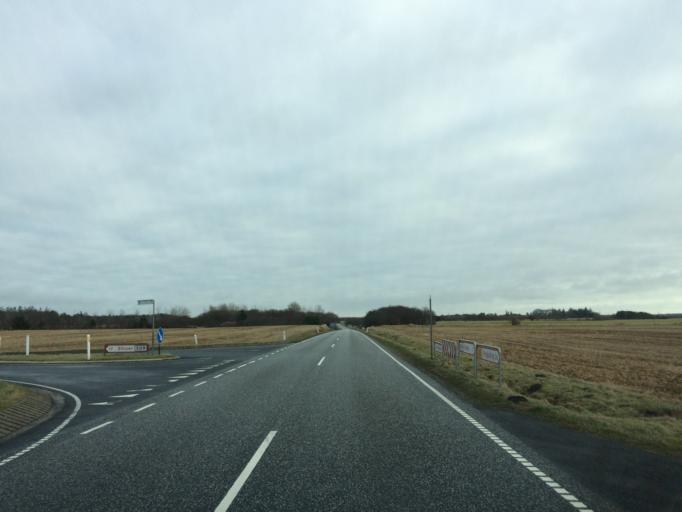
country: DK
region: Central Jutland
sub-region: Holstebro Kommune
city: Ulfborg
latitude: 56.3666
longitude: 8.4393
